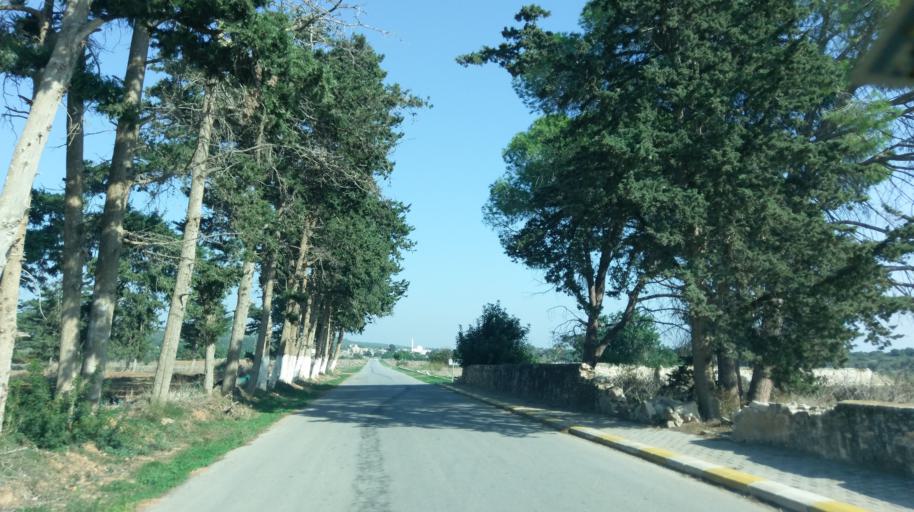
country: CY
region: Ammochostos
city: Leonarisso
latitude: 35.4742
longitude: 34.1559
